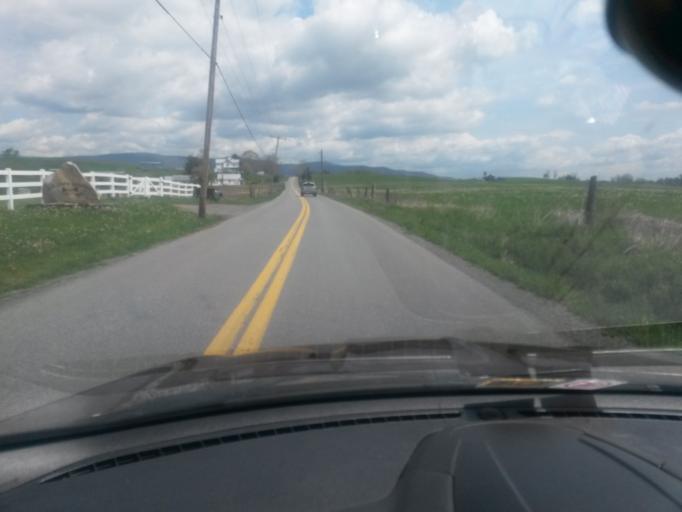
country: US
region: West Virginia
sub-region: Pocahontas County
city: Marlinton
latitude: 38.1225
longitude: -80.2149
